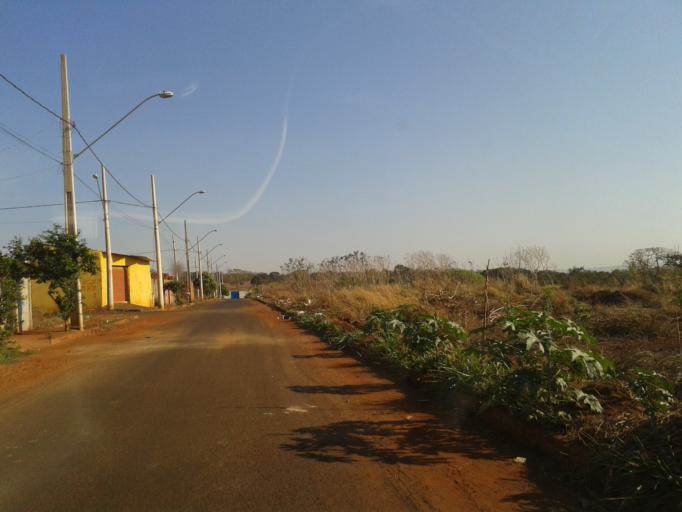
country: BR
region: Minas Gerais
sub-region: Ituiutaba
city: Ituiutaba
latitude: -18.9861
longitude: -49.4242
